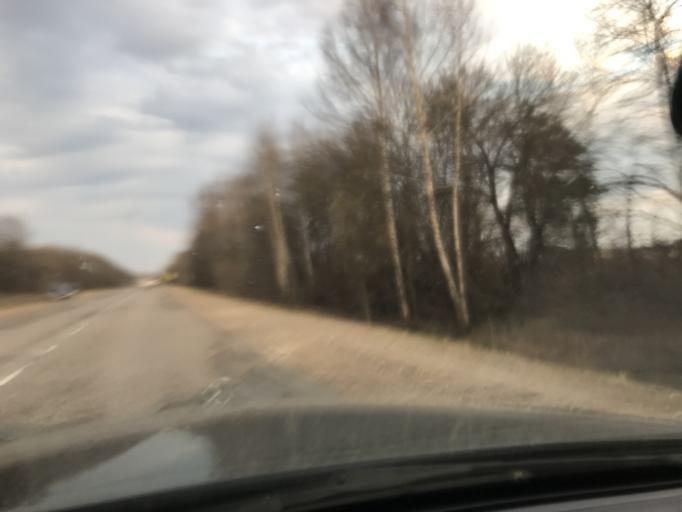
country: RU
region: Vladimir
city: Murom
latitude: 55.6190
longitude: 41.9224
